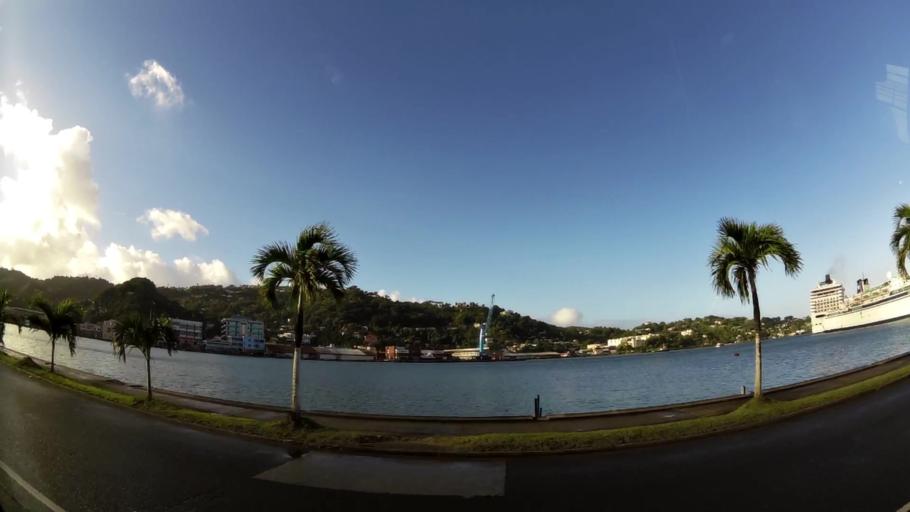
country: LC
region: Castries Quarter
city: Bisee
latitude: 14.0140
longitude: -60.9912
